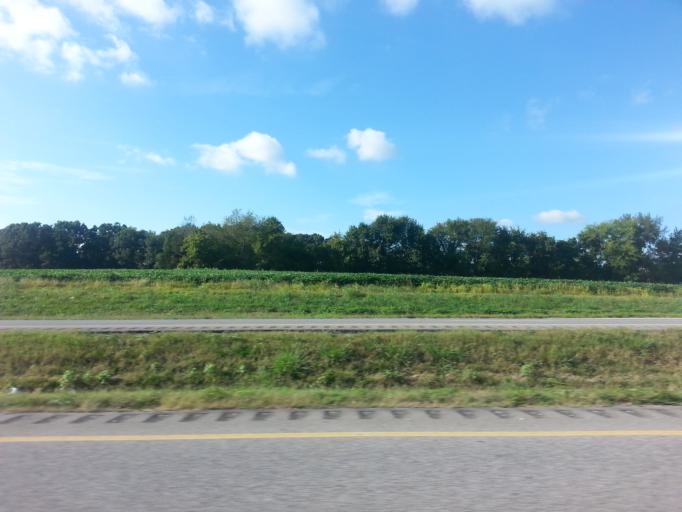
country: US
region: Alabama
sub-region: Colbert County
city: Tuscumbia
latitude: 34.7097
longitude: -87.7349
